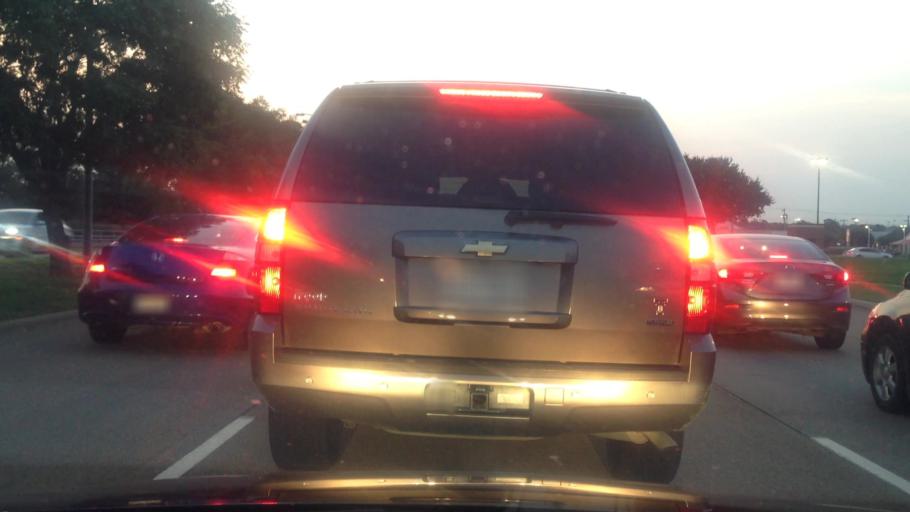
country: US
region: Texas
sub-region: Tarrant County
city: Colleyville
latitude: 32.8619
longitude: -97.1894
